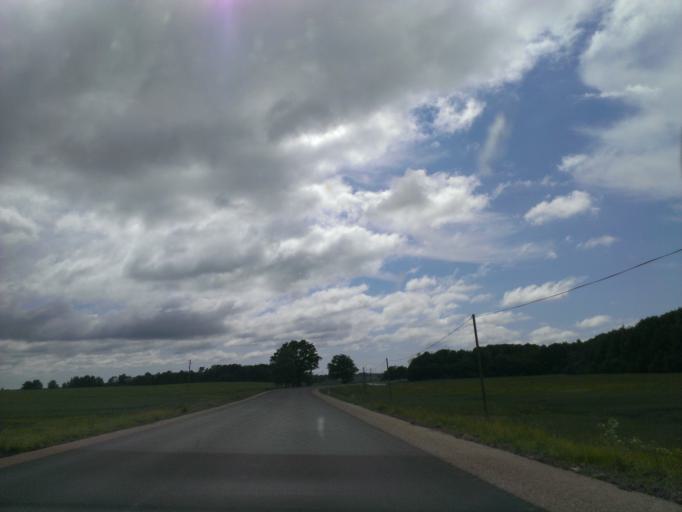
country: LV
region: Durbe
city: Liegi
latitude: 56.5798
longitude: 21.3160
